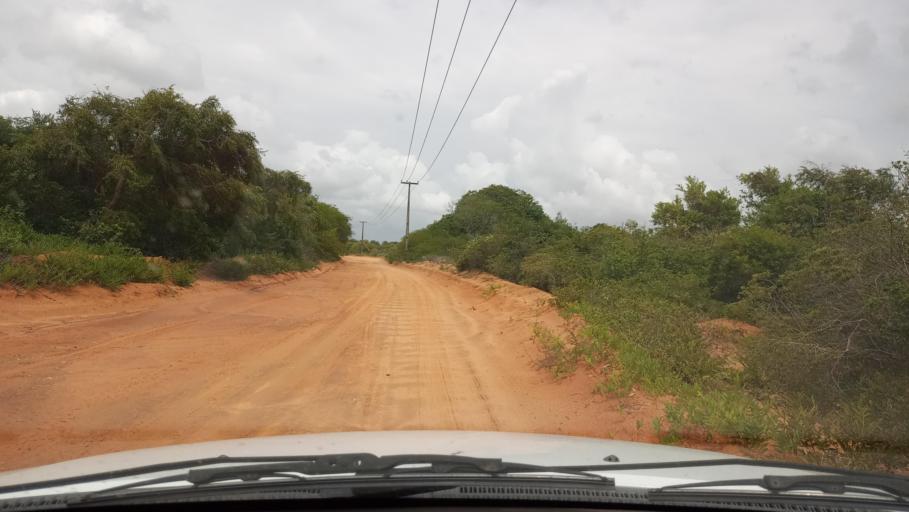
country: BR
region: Rio Grande do Norte
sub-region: Maxaranguape
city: Sao Miguel
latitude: -5.4831
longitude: -35.3179
